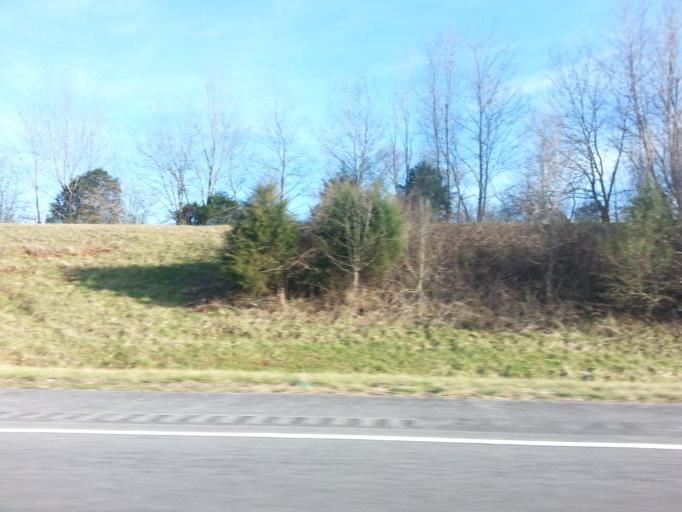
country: US
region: Tennessee
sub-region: Warren County
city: McMinnville
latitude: 35.7387
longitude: -85.6534
